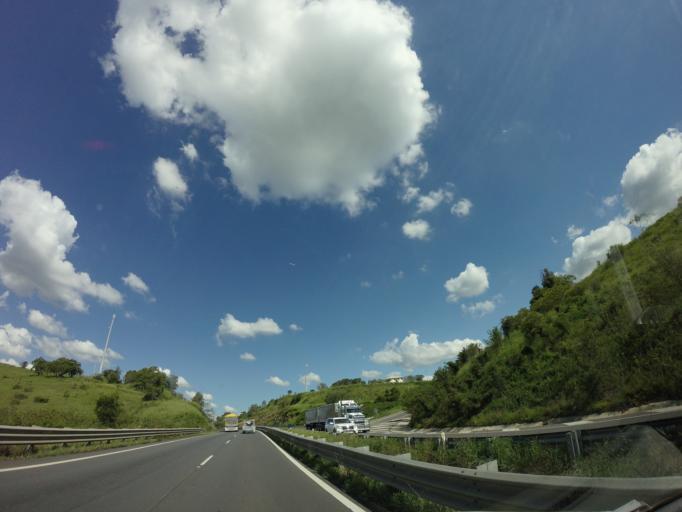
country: AU
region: Queensland
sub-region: Ipswich
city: Thagoona
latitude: -27.5649
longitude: 152.5640
